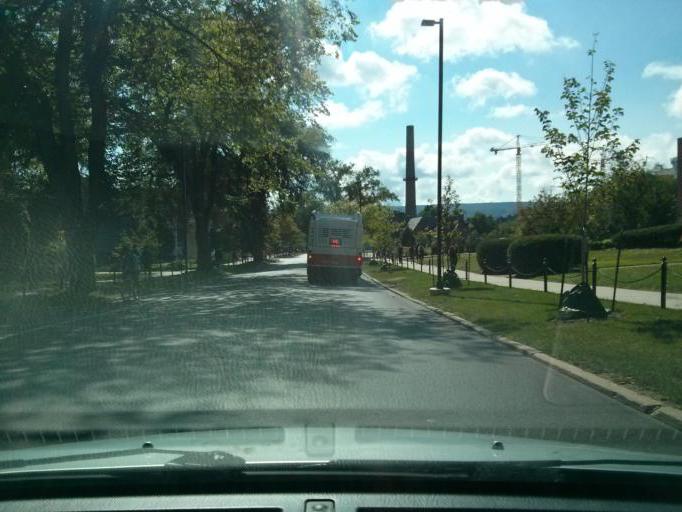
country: US
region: Pennsylvania
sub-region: Centre County
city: State College
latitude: 40.7954
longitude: -77.8676
